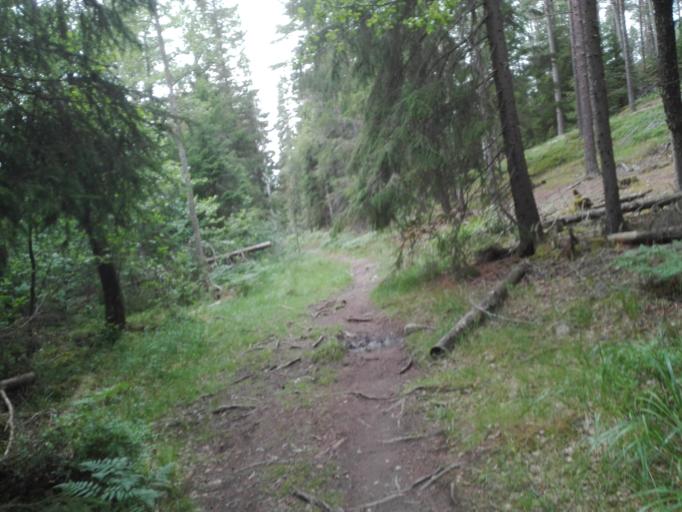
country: SE
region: Stockholm
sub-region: Nacka Kommun
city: Fisksatra
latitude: 59.2812
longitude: 18.2502
